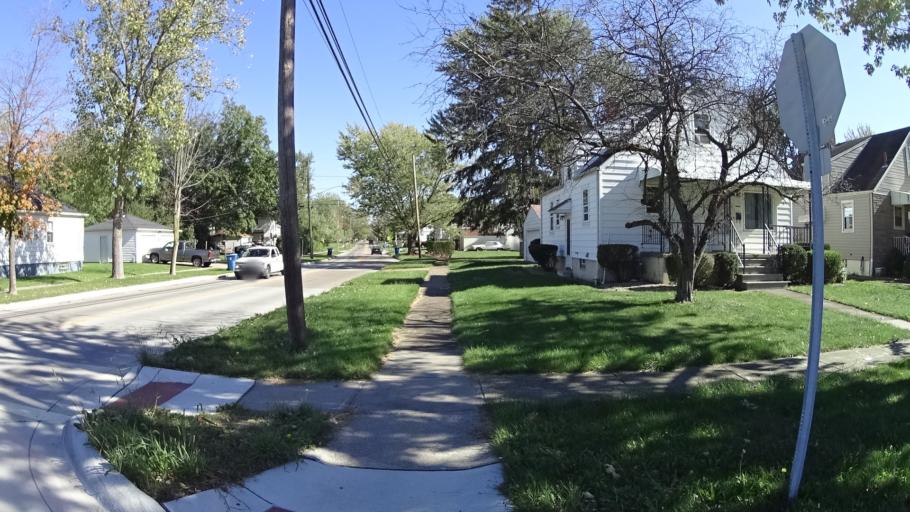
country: US
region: Ohio
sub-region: Lorain County
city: Lorain
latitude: 41.4399
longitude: -82.1698
